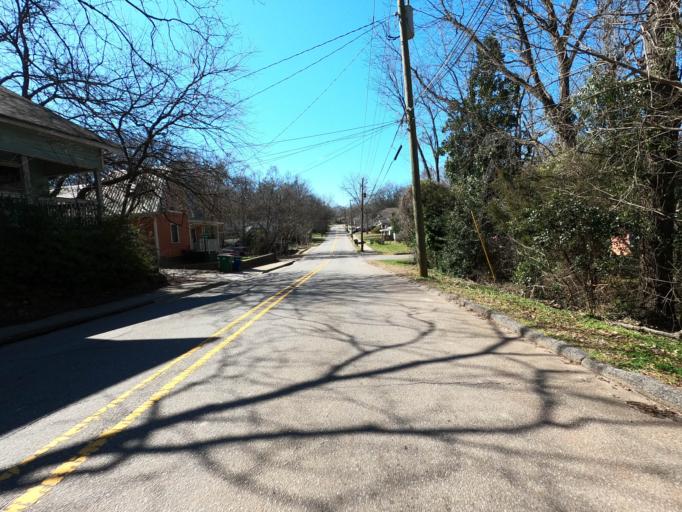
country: US
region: Georgia
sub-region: Clarke County
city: Athens
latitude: 33.9679
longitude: -83.3829
